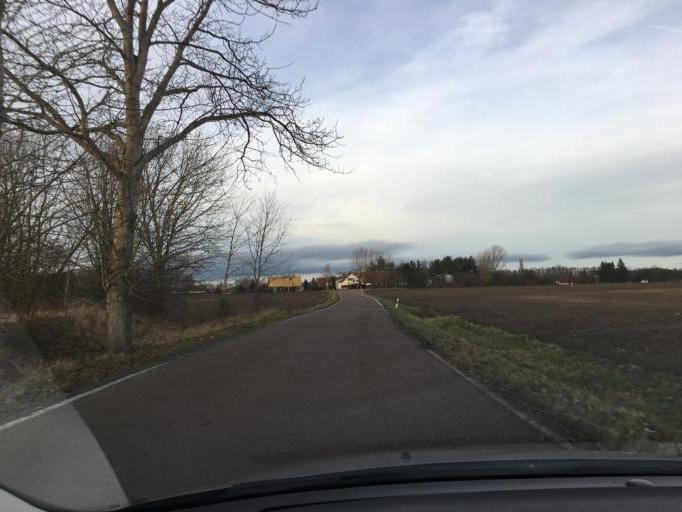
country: DE
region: Saxony
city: Grossposna
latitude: 51.2378
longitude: 12.4844
